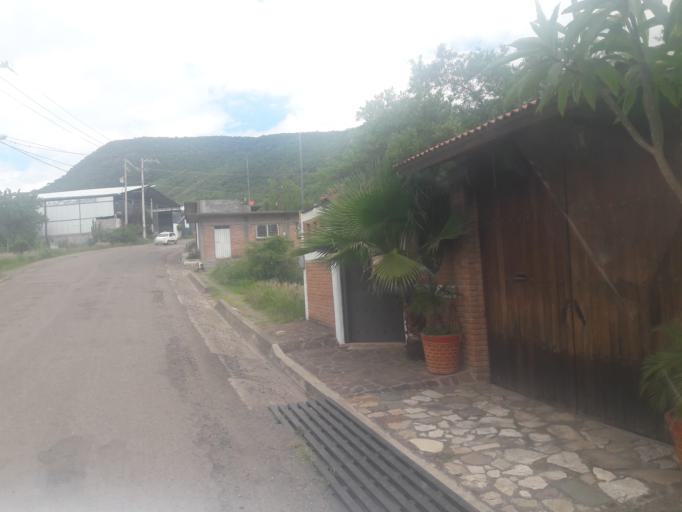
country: MX
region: Oaxaca
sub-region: Heroica Ciudad de Huajuapan de Leon
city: La Junta
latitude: 17.8276
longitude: -97.7495
